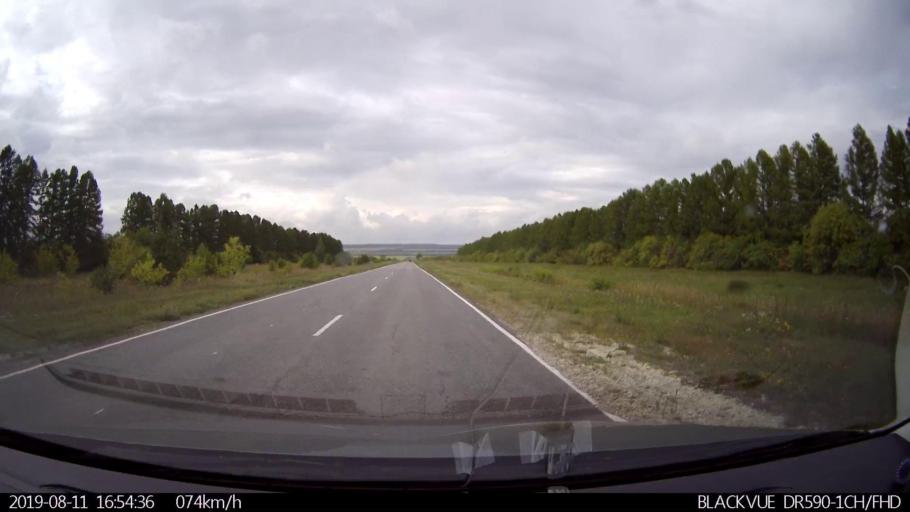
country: RU
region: Ulyanovsk
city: Mayna
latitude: 54.2744
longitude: 47.6660
